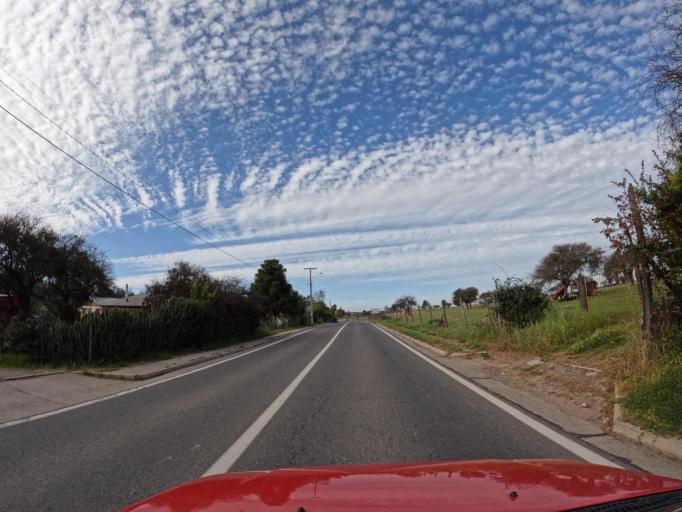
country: CL
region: O'Higgins
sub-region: Provincia de Colchagua
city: Santa Cruz
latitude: -34.2224
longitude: -71.7220
